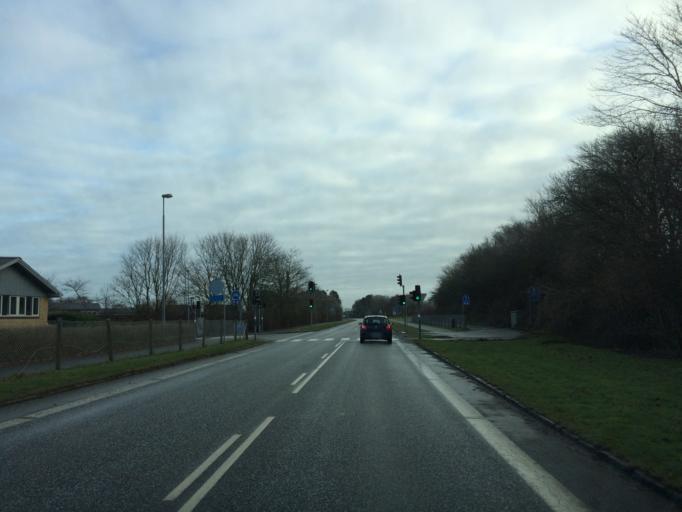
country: DK
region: Central Jutland
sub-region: Struer Kommune
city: Struer
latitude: 56.4899
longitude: 8.5713
